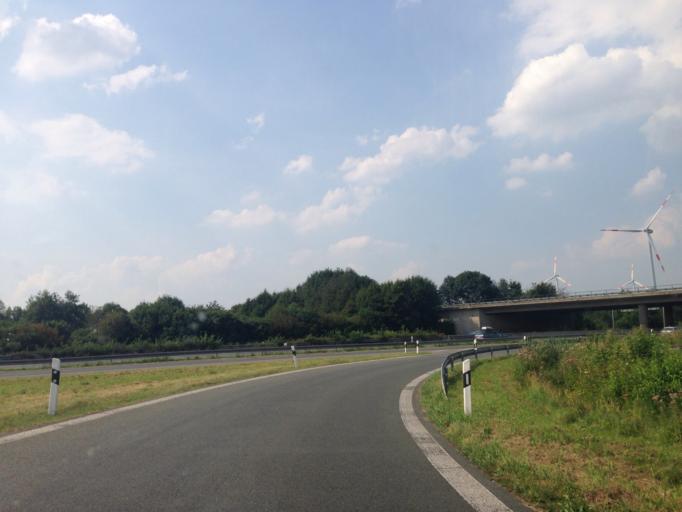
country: DE
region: North Rhine-Westphalia
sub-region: Regierungsbezirk Munster
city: Ochtrup
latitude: 52.1909
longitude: 7.1163
